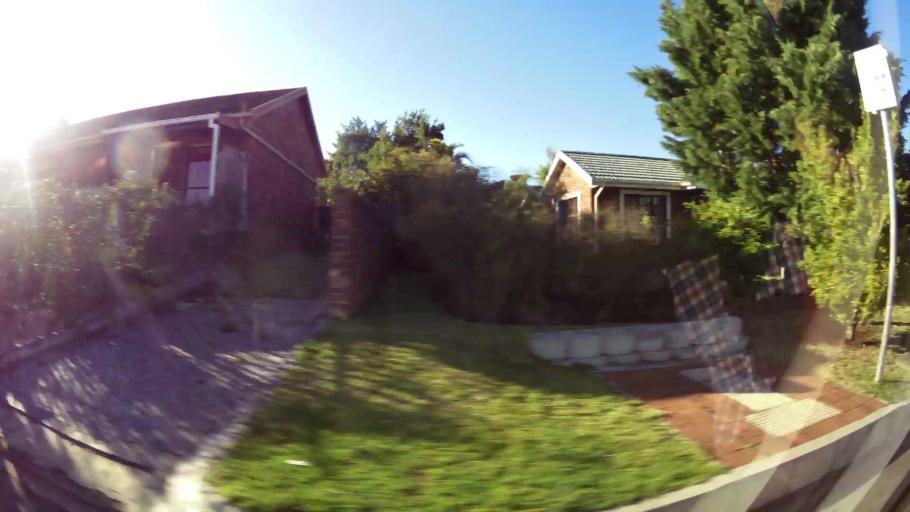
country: ZA
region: Western Cape
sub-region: Eden District Municipality
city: George
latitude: -33.9679
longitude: 22.4378
